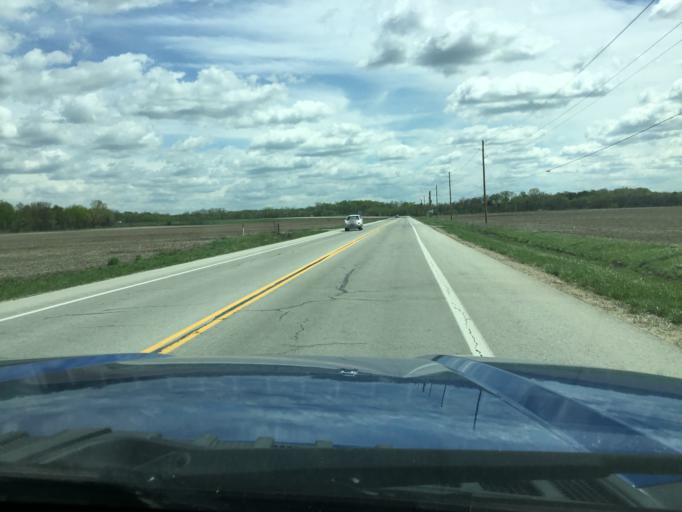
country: US
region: Kansas
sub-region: Douglas County
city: Lawrence
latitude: 38.9127
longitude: -95.2665
